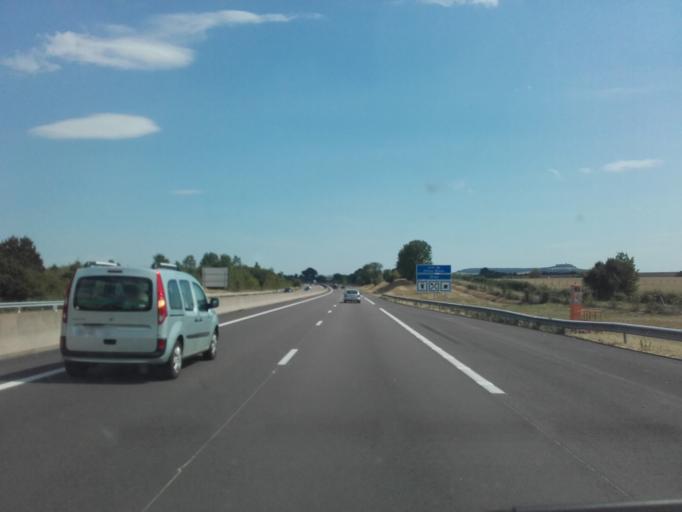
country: FR
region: Bourgogne
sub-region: Departement de la Cote-d'Or
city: Semur-en-Auxois
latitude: 47.4277
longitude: 4.3176
